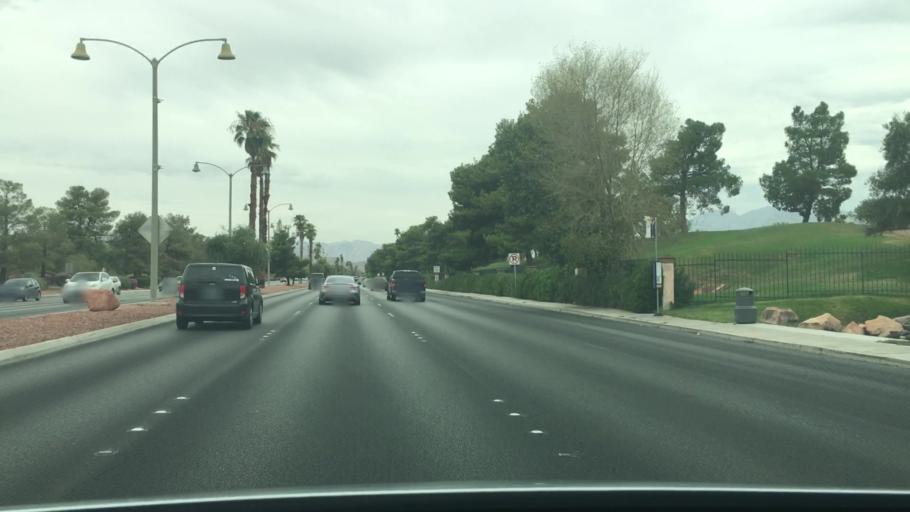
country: US
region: Nevada
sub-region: Clark County
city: Spring Valley
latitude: 36.1442
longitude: -115.2830
